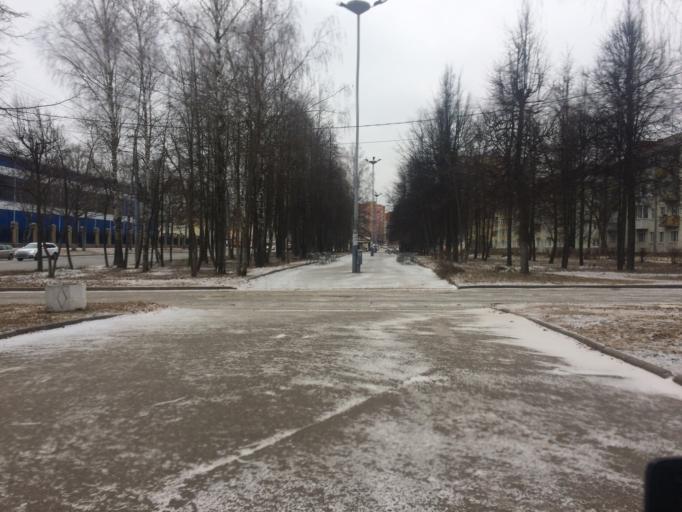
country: RU
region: Mariy-El
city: Yoshkar-Ola
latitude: 56.6424
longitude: 47.8723
